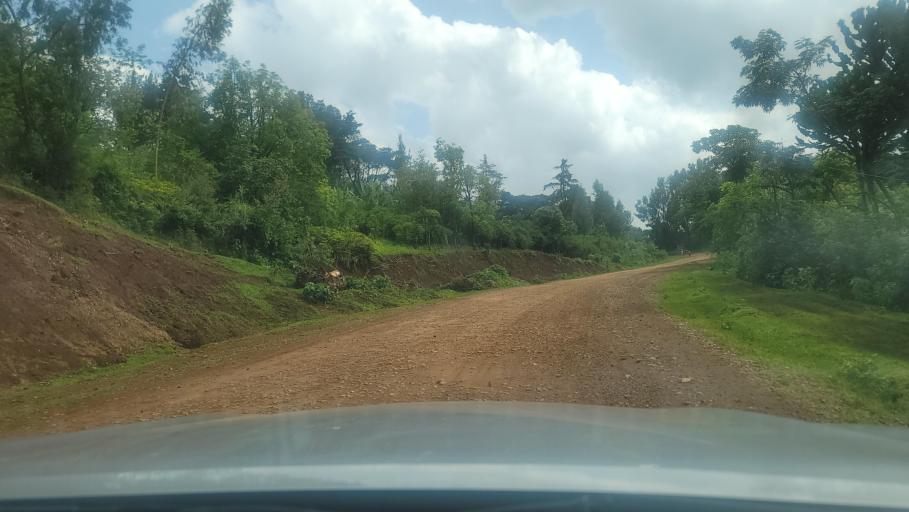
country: ET
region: Oromiya
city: Agaro
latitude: 7.8032
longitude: 36.4650
